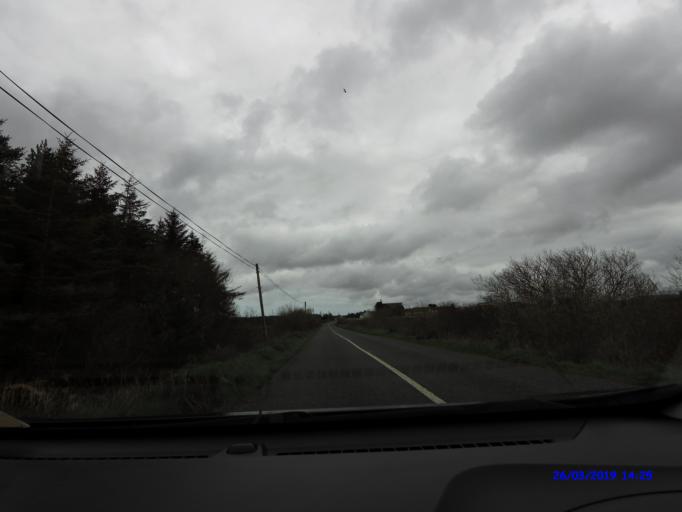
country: IE
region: Connaught
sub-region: Maigh Eo
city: Belmullet
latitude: 54.2410
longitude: -9.6555
